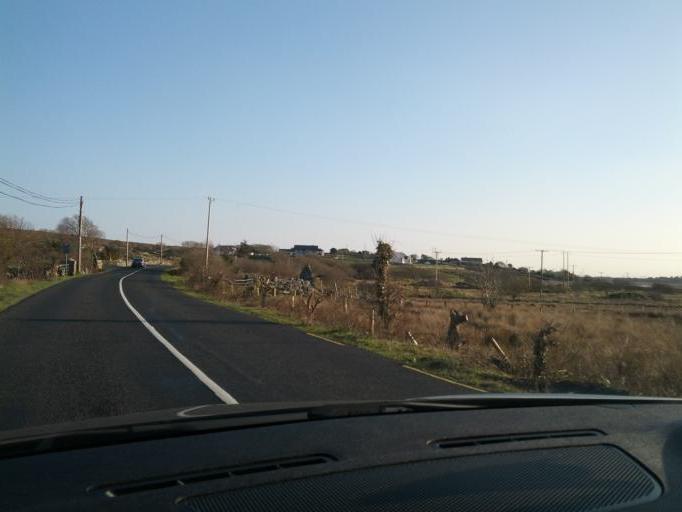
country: IE
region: Connaught
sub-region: County Galway
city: Oughterard
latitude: 53.3239
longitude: -9.5460
